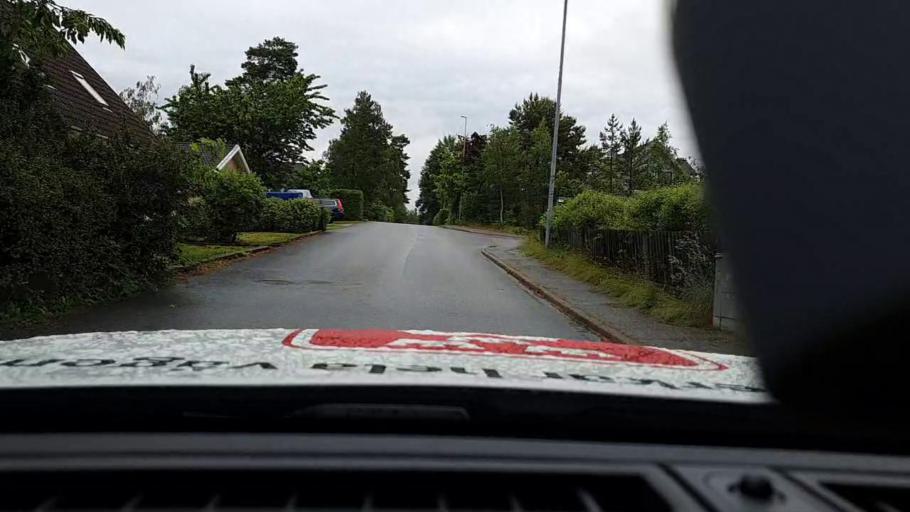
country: SE
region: Stockholm
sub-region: Taby Kommun
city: Taby
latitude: 59.4436
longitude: 18.0276
